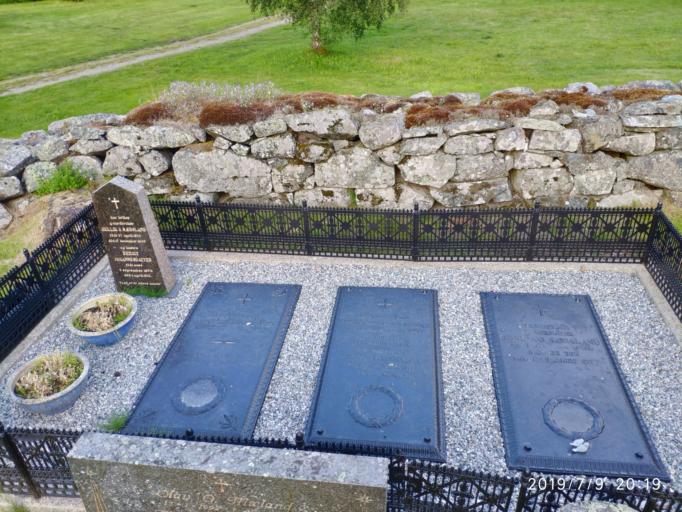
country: NO
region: Telemark
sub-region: Seljord
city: Seljord
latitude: 59.6038
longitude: 8.6384
